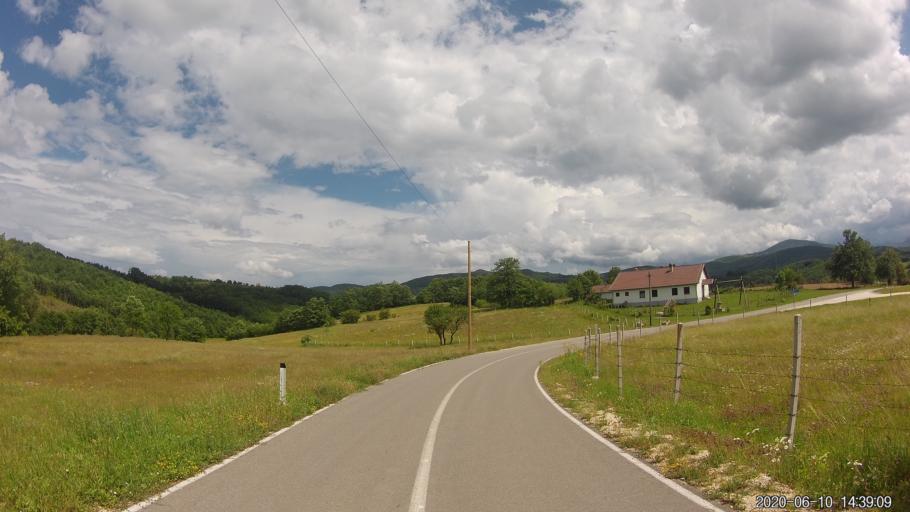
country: XK
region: Prizren
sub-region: Komuna e Therandes
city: Budakovo
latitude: 42.4020
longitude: 20.9443
